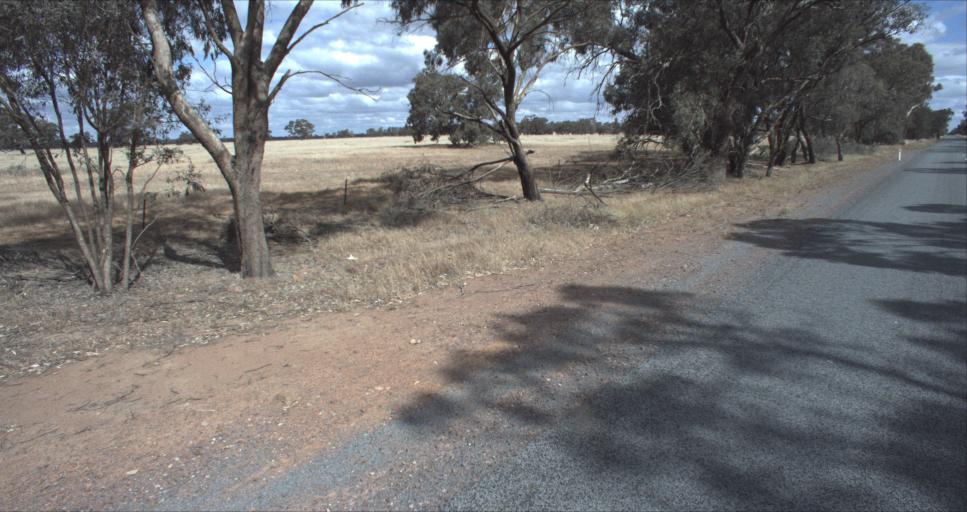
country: AU
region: New South Wales
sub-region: Leeton
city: Leeton
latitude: -34.6640
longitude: 146.3488
